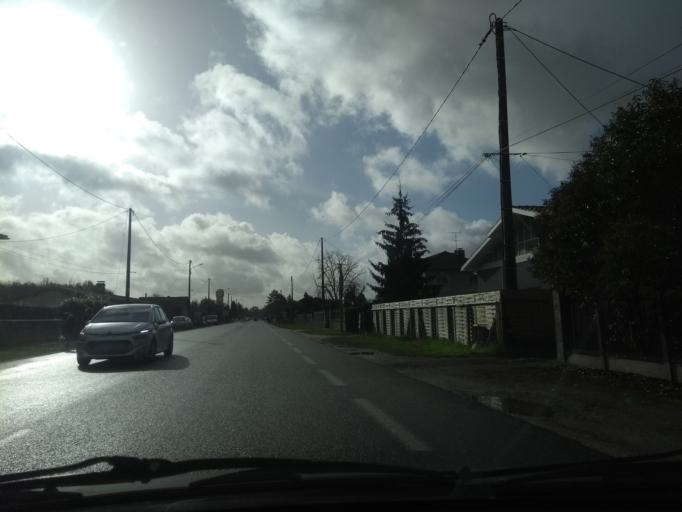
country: FR
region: Aquitaine
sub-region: Departement de la Gironde
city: Belin-Beliet
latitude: 44.5052
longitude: -0.7891
